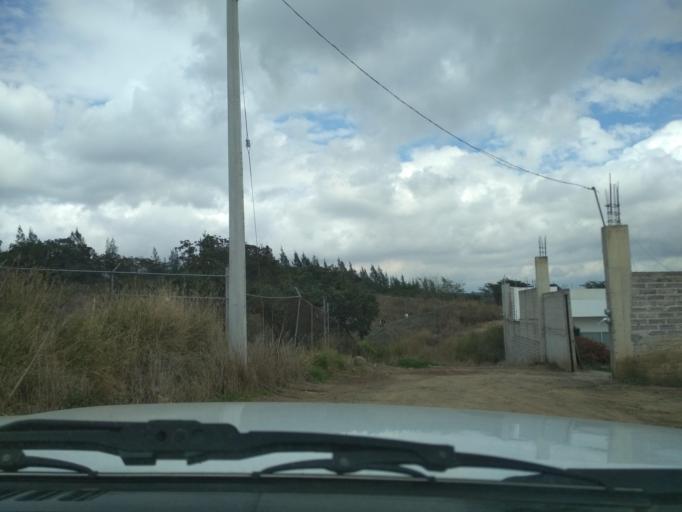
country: MX
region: Veracruz
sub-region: Emiliano Zapata
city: Dos Rios
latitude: 19.5021
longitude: -96.8229
